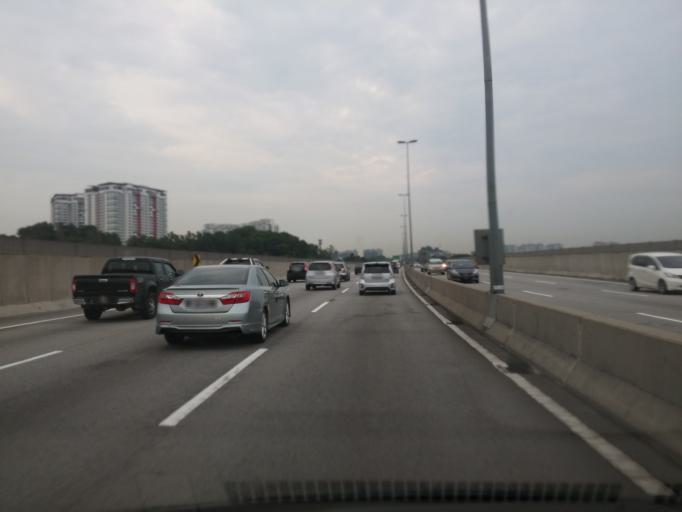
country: MY
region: Kuala Lumpur
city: Kuala Lumpur
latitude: 3.0704
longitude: 101.6859
